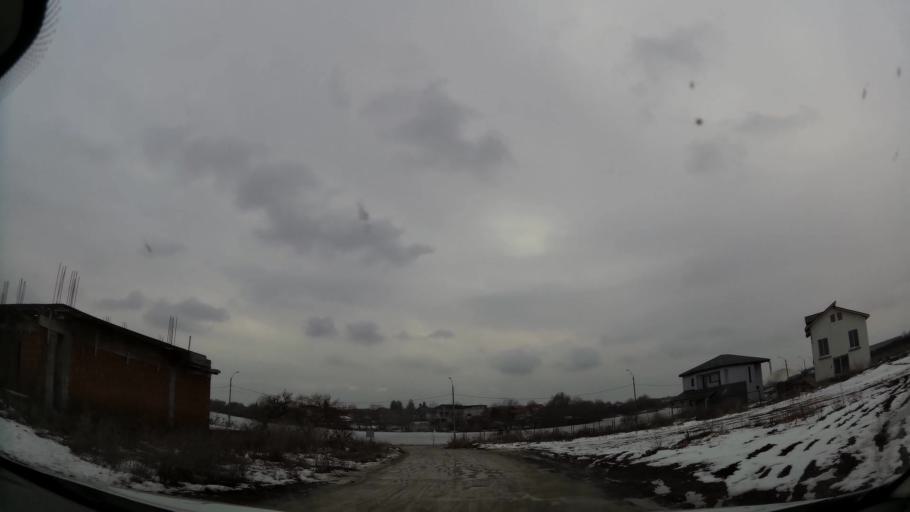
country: RO
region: Ilfov
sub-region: Comuna Tunari
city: Tunari
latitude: 44.5542
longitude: 26.1507
